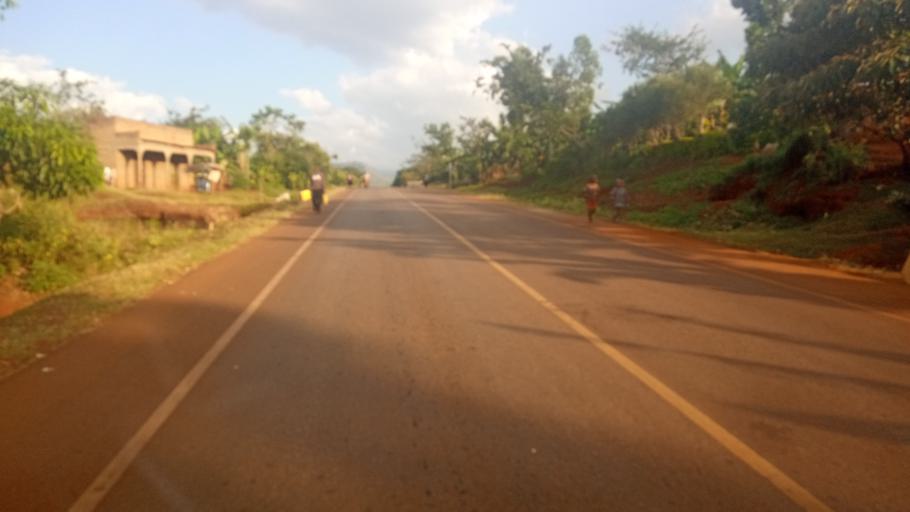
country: UG
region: Eastern Region
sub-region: Sironko District
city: Sironko
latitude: 1.3238
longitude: 34.3315
